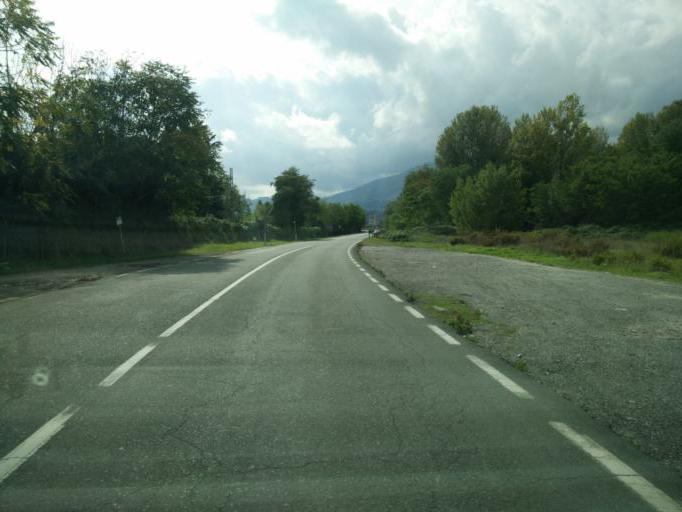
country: IT
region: Tuscany
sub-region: Provincia di Massa-Carrara
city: Filattiera
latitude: 44.3450
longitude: 9.9118
